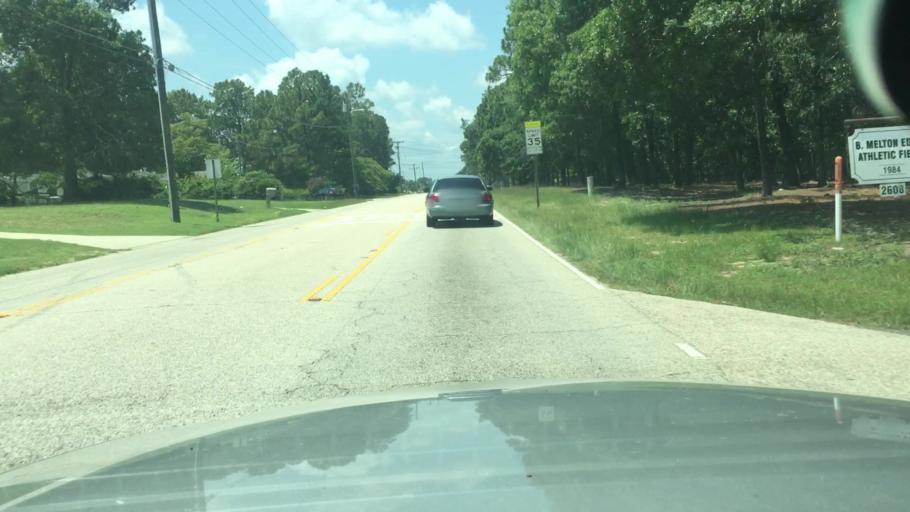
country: US
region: North Carolina
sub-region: Cumberland County
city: Fayetteville
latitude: 35.0208
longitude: -78.9084
